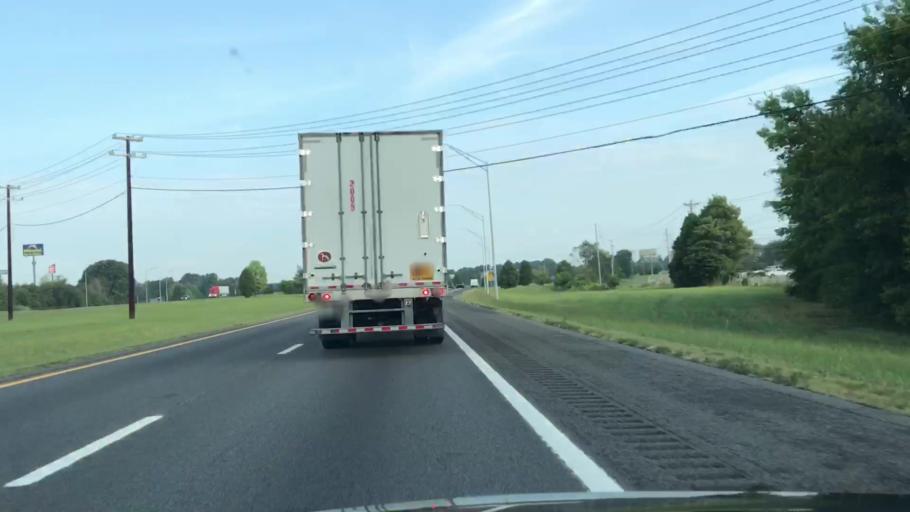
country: US
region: Tennessee
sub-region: Montgomery County
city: Clarksville
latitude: 36.5966
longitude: -87.2770
